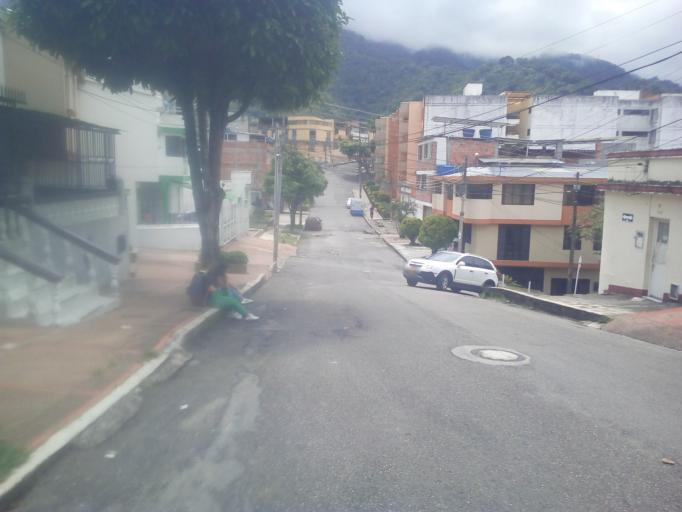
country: CO
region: Tolima
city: Ibague
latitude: 4.4491
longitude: -75.2424
